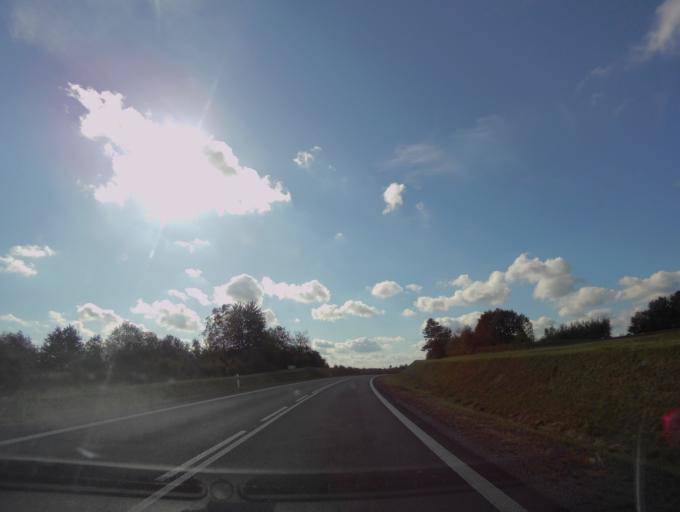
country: PL
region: Subcarpathian Voivodeship
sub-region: Powiat lezajski
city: Lezajsk
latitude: 50.2494
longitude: 22.4083
